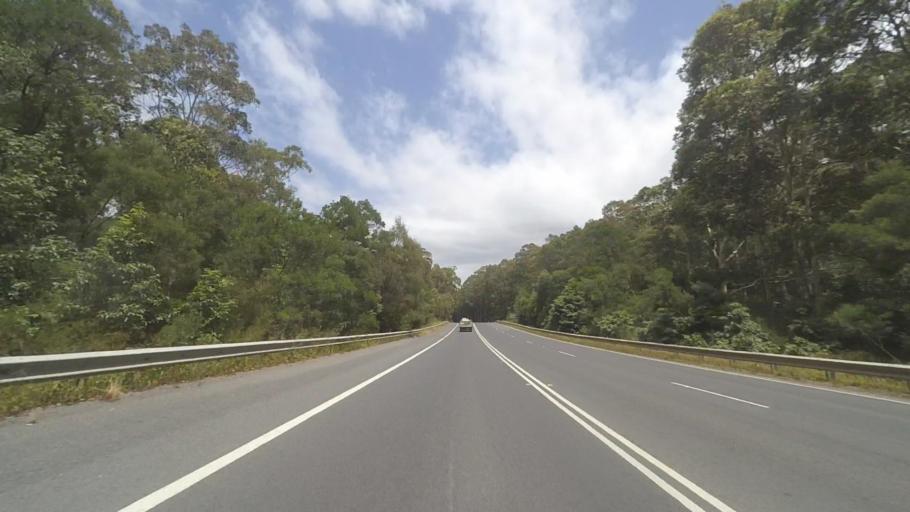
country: AU
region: New South Wales
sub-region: Shoalhaven Shire
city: Falls Creek
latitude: -35.0759
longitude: 150.5581
